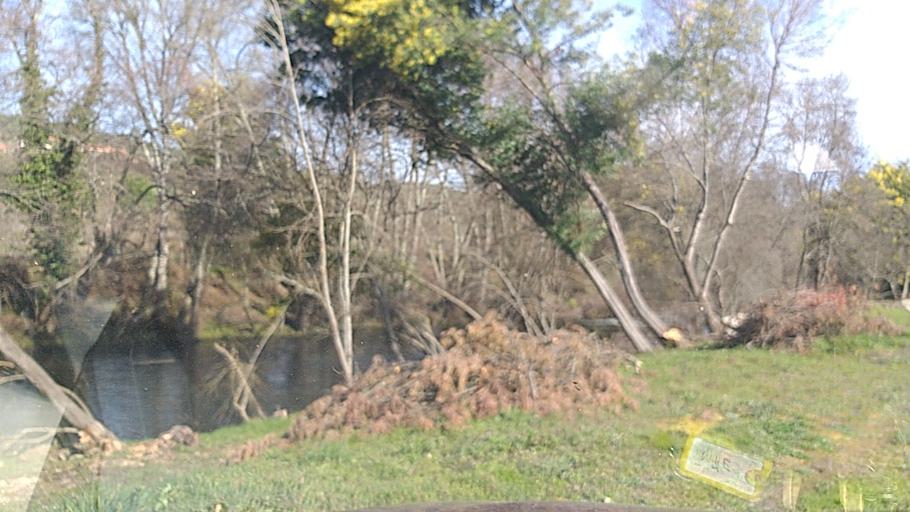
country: PT
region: Guarda
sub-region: Fornos de Algodres
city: Fornos de Algodres
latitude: 40.6096
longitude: -7.5247
